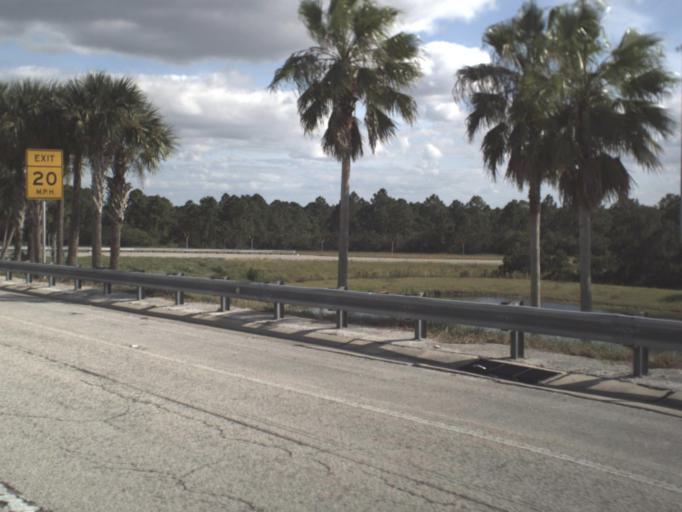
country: US
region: Florida
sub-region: Brevard County
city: Sharpes
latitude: 28.4116
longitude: -80.8193
